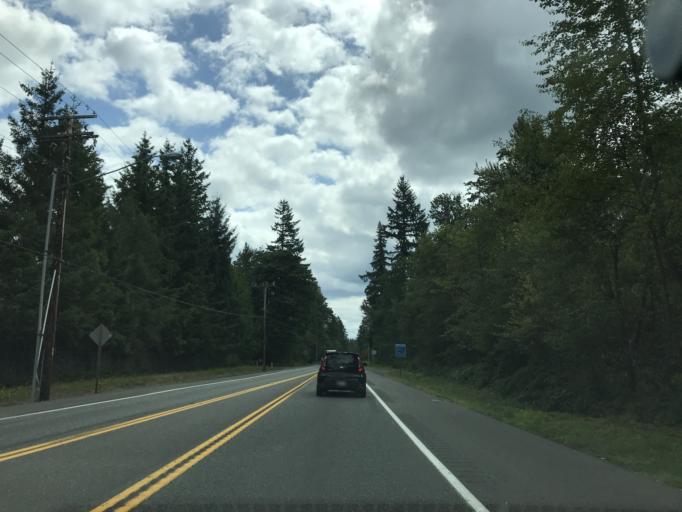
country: US
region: Washington
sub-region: King County
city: Maple Heights-Lake Desire
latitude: 47.4368
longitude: -122.1163
